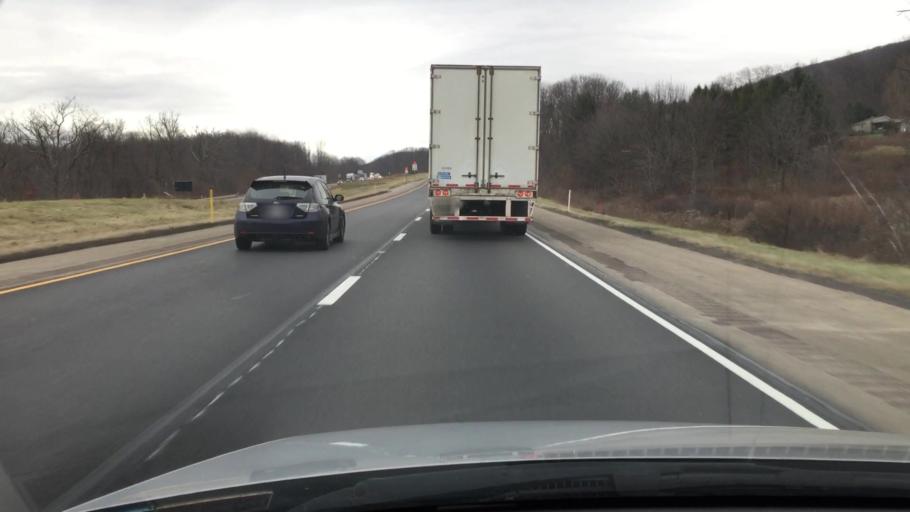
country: US
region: Pennsylvania
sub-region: Luzerne County
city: Nescopeck
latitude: 41.0109
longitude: -76.2298
